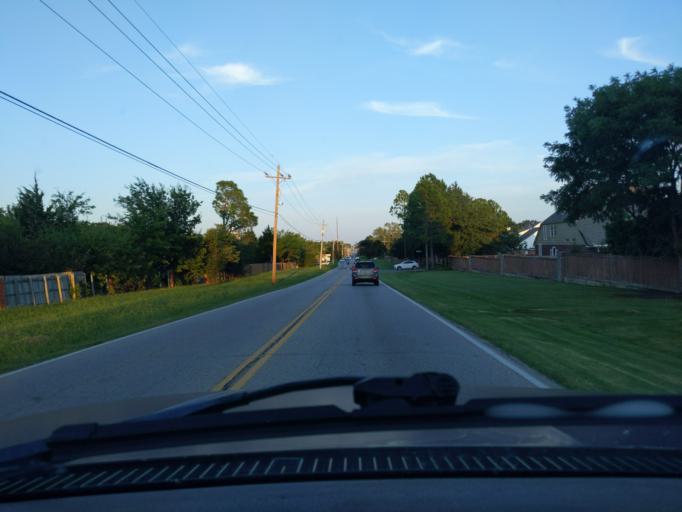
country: US
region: Oklahoma
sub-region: Tulsa County
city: Jenks
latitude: 36.0464
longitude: -95.8982
